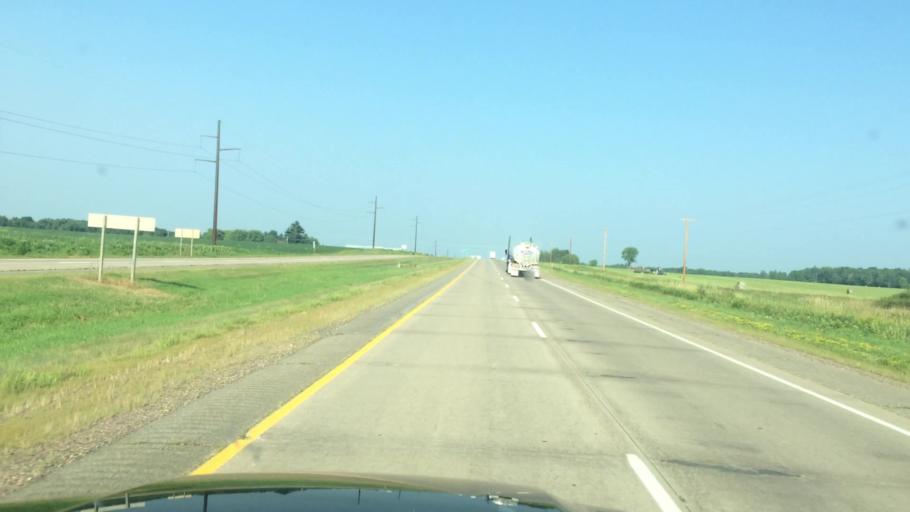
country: US
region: Wisconsin
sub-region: Marathon County
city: Edgar
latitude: 44.9444
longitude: -89.9969
